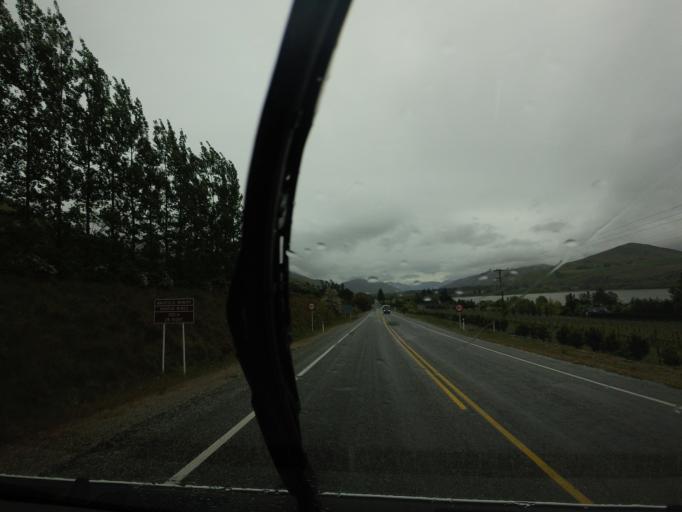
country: NZ
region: Otago
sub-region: Queenstown-Lakes District
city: Arrowtown
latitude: -44.9856
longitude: 168.8189
